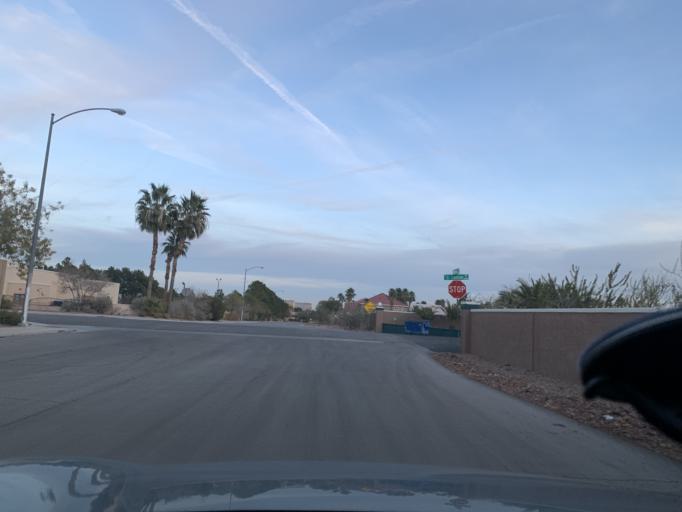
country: US
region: Nevada
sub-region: Clark County
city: Spring Valley
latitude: 36.0907
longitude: -115.2299
